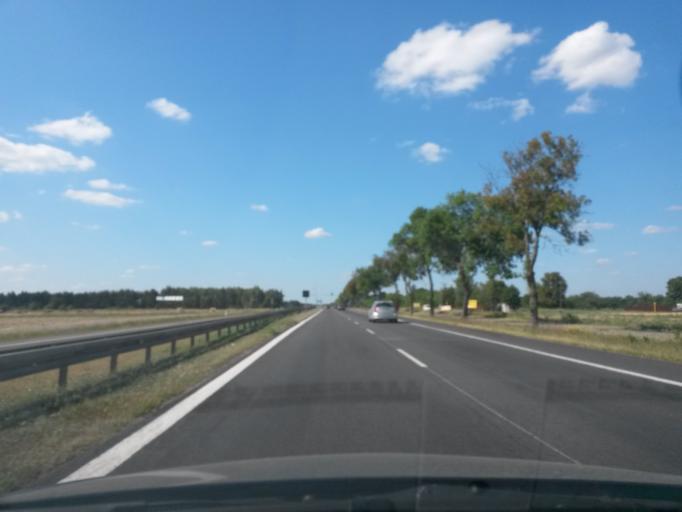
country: PL
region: Masovian Voivodeship
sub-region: Powiat plonski
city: Zaluski
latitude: 52.5581
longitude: 20.4944
